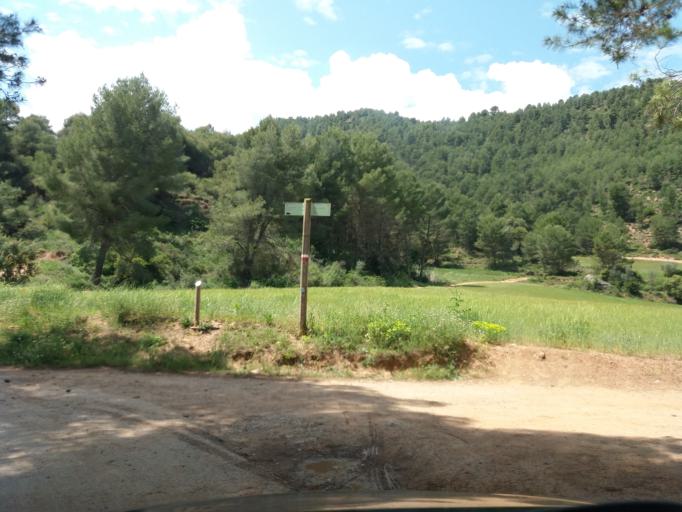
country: ES
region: Catalonia
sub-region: Provincia de Barcelona
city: Sant Joan de Vilatorrada
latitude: 41.7443
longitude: 1.7878
